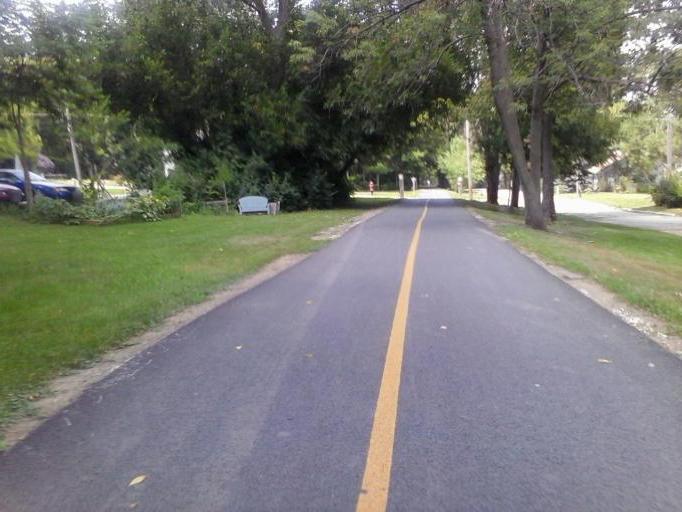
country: US
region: Illinois
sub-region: Kane County
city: North Aurora
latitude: 41.7966
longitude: -88.3219
